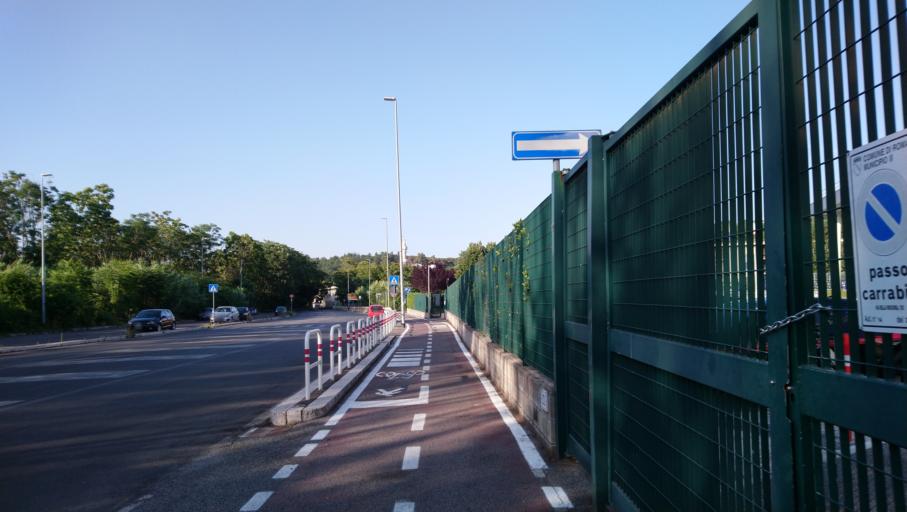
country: IT
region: Latium
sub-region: Citta metropolitana di Roma Capitale
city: Rome
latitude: 41.9326
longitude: 12.4919
